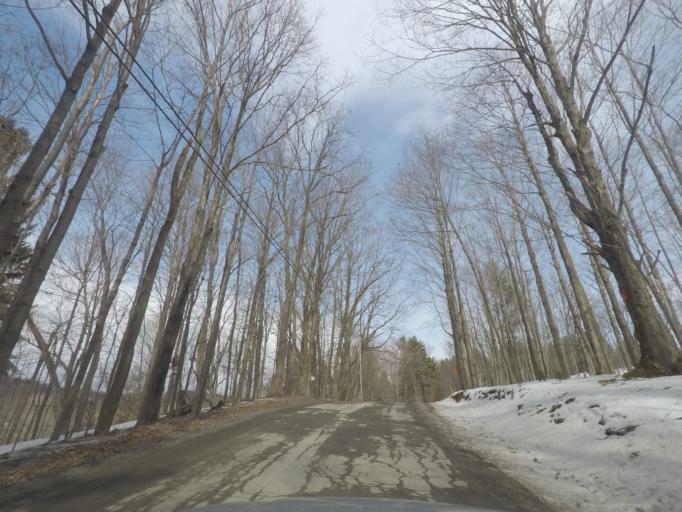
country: US
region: New York
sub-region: Saratoga County
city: Waterford
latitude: 42.7758
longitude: -73.6039
